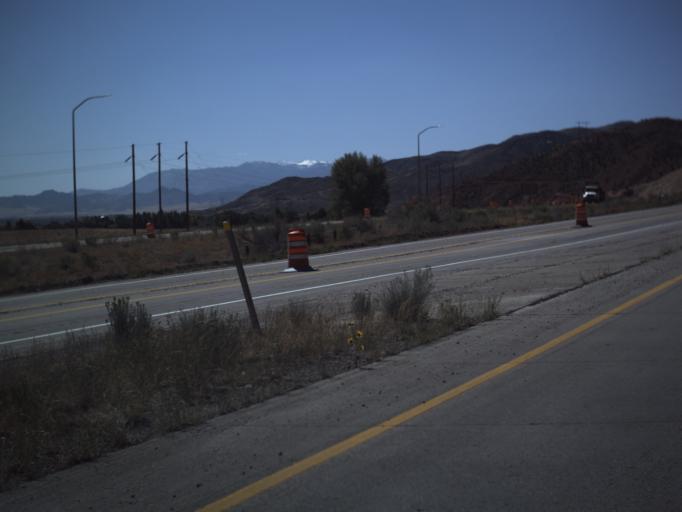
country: US
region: Utah
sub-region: Sevier County
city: Richfield
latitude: 38.7883
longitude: -112.0878
